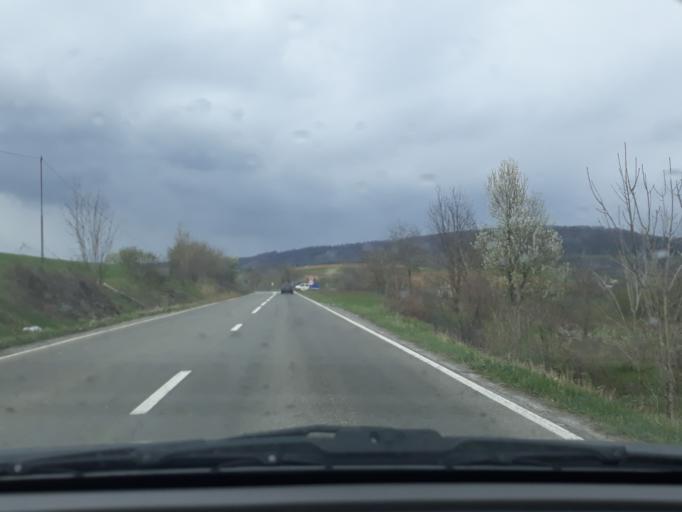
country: RO
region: Harghita
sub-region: Comuna Lupeni
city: Lupeni
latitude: 46.3924
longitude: 25.2147
